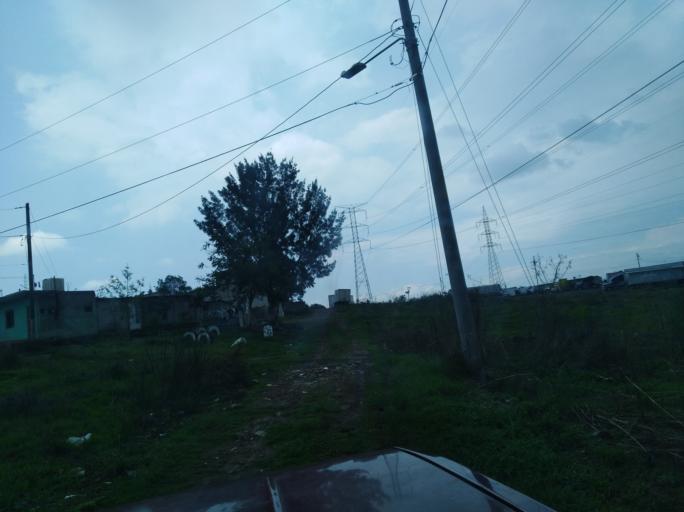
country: GT
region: Guatemala
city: Villa Nueva
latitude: 14.5223
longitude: -90.6226
